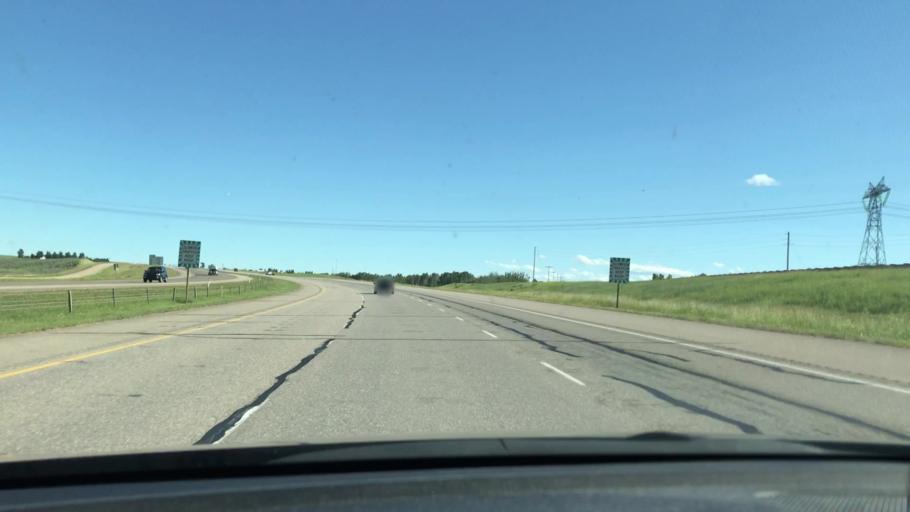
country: CA
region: Alberta
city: Crossfield
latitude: 51.4636
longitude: -114.0250
